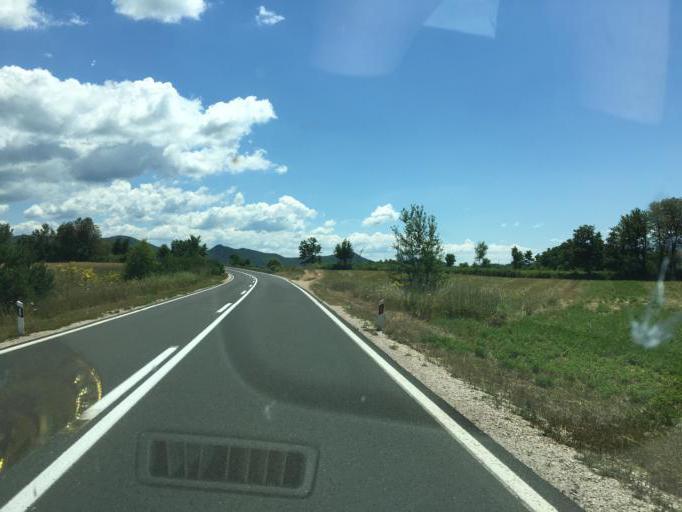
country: HR
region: Licko-Senjska
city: Gospic
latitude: 44.5759
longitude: 15.4056
